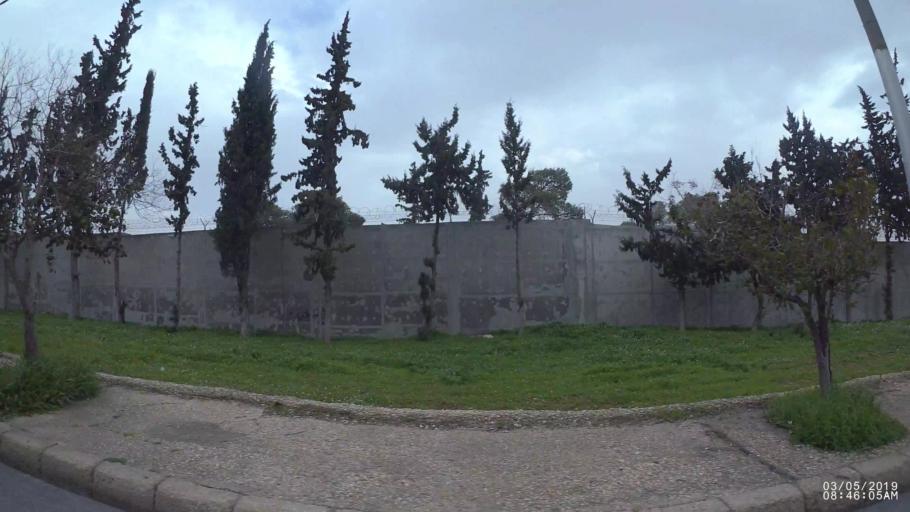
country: JO
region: Amman
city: Amman
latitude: 31.9602
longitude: 35.9418
